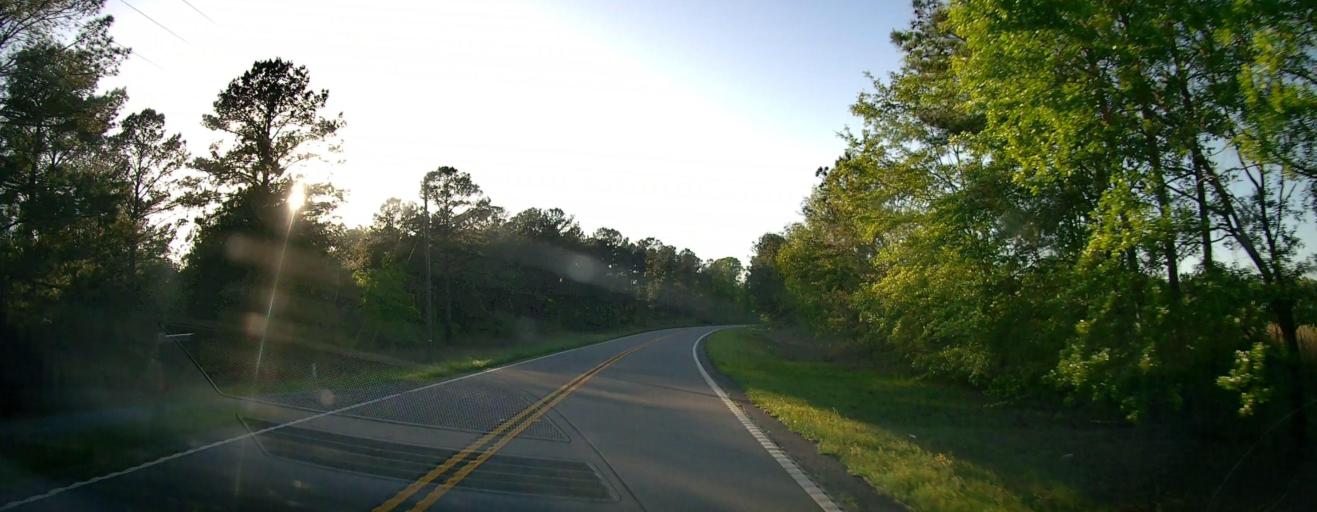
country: US
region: Georgia
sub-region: Schley County
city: Ellaville
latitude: 32.3332
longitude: -84.3481
